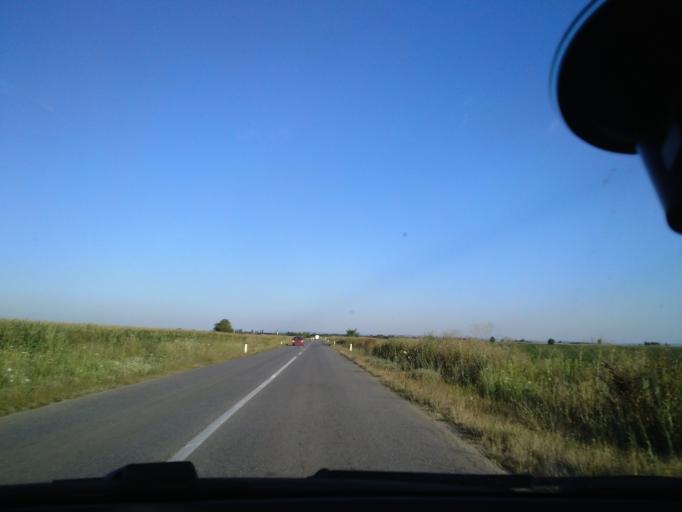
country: RS
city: Obrovac
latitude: 45.4306
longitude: 19.3824
